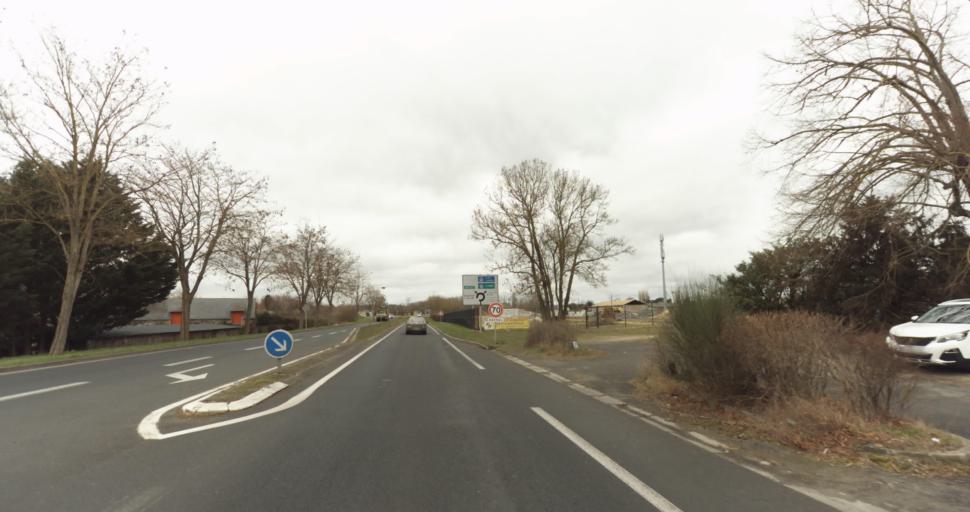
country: FR
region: Pays de la Loire
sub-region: Departement de Maine-et-Loire
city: Jumelles
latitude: 47.3870
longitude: -0.1144
